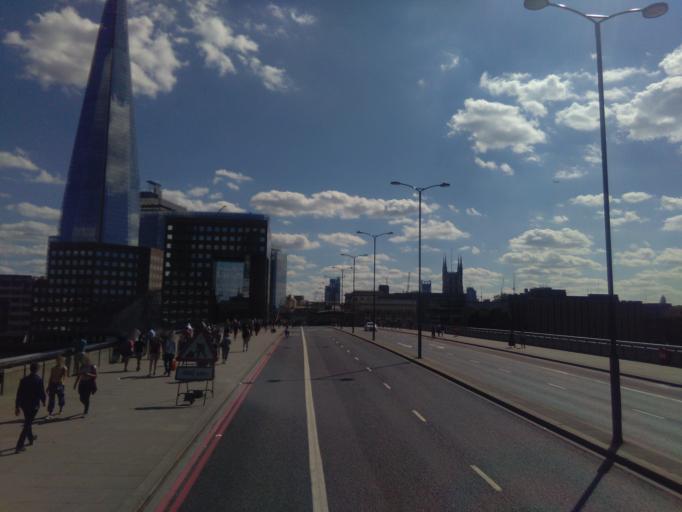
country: GB
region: England
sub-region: Greater London
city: City of London
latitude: 51.5089
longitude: -0.0873
